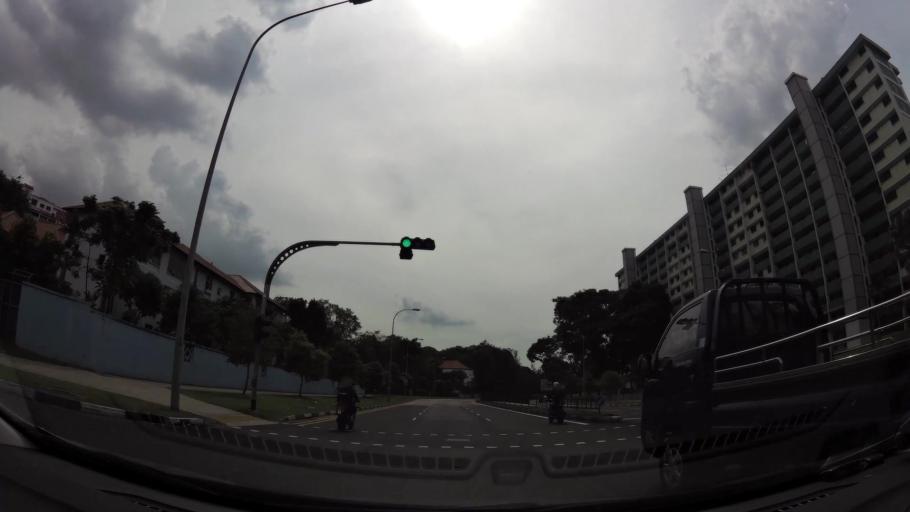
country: MY
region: Johor
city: Johor Bahru
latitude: 1.4418
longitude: 103.7751
